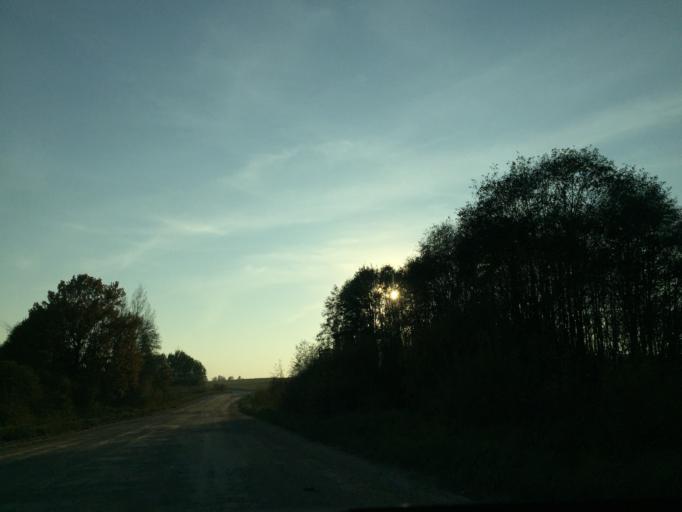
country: LV
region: Vainode
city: Vainode
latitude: 56.5625
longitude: 21.8469
